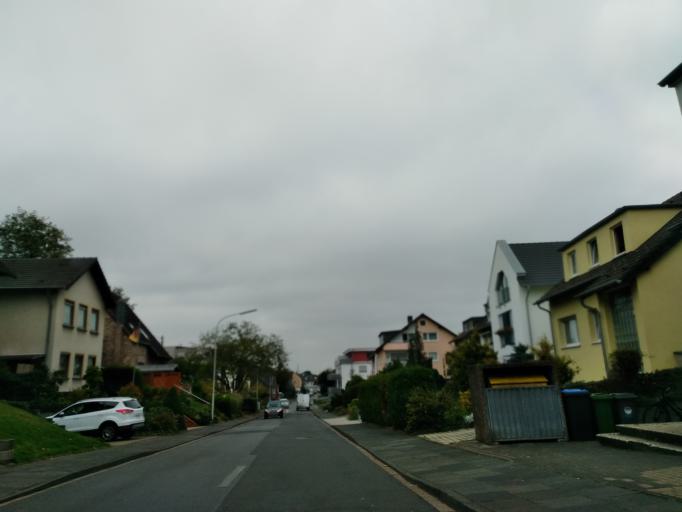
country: DE
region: North Rhine-Westphalia
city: Sankt Augustin
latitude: 50.7442
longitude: 7.1731
